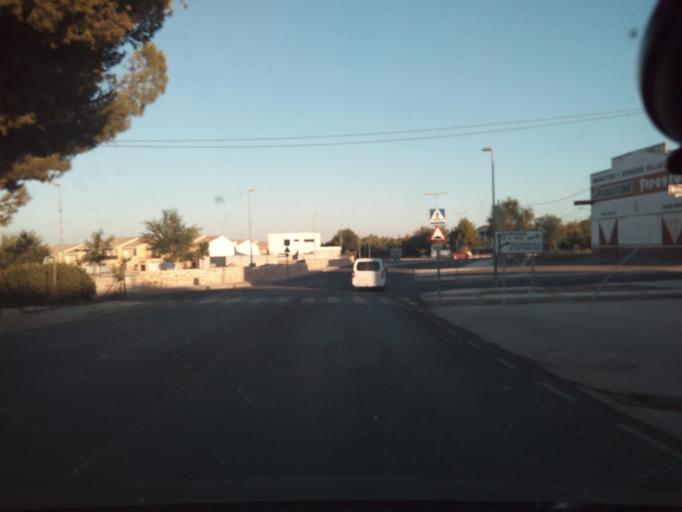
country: ES
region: Castille-La Mancha
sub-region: Province of Toledo
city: Villacanas
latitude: 39.6148
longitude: -3.3373
